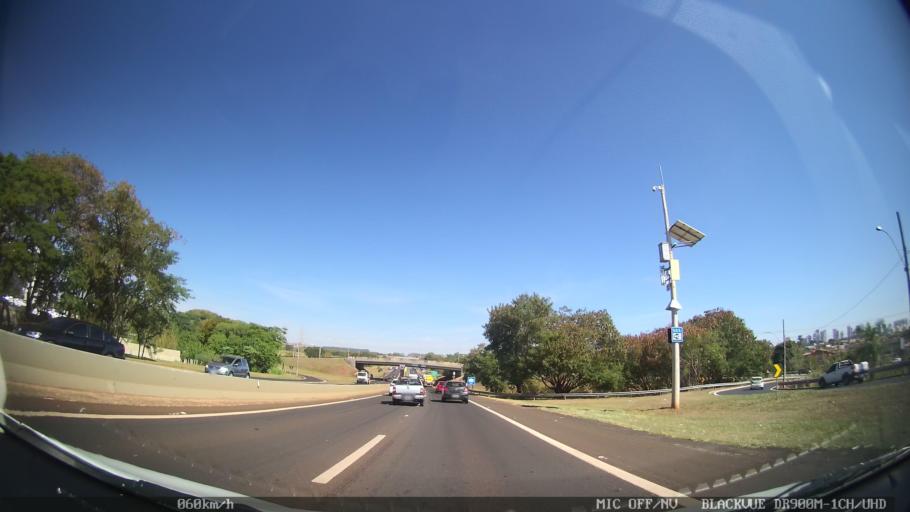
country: BR
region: Sao Paulo
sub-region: Ribeirao Preto
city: Ribeirao Preto
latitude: -21.2138
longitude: -47.7725
